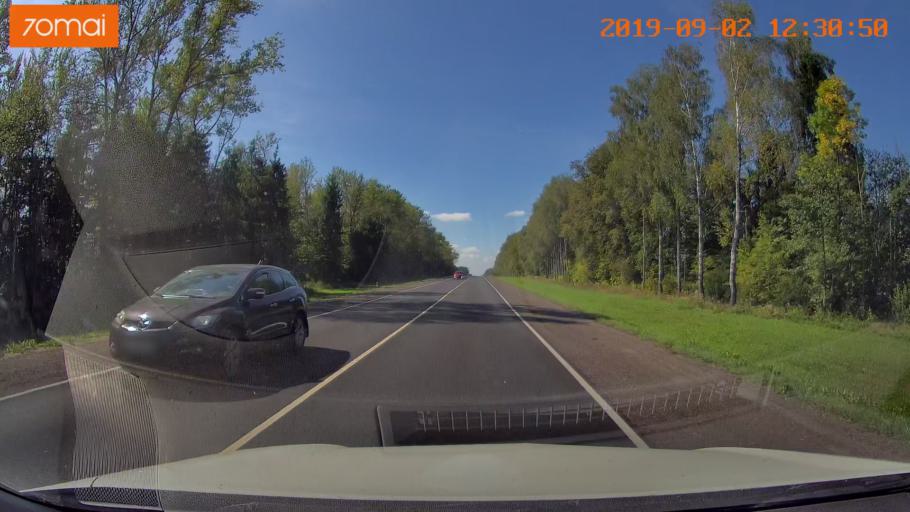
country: RU
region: Smolensk
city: Shumyachi
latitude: 53.8292
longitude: 32.4652
